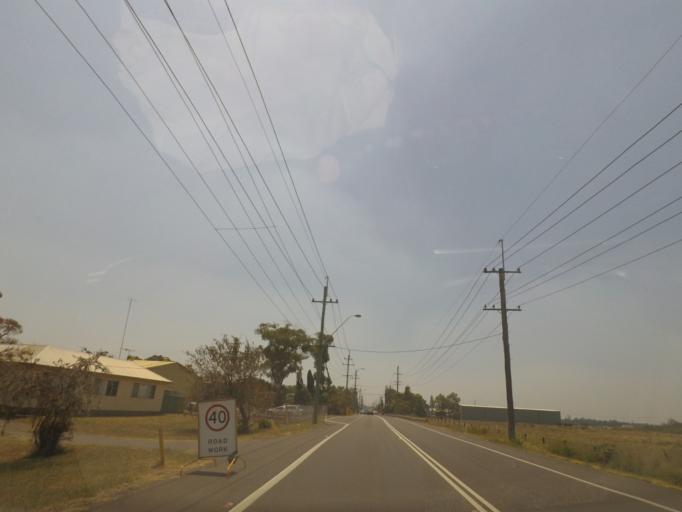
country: AU
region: New South Wales
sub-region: Newcastle
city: Mayfield West
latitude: -32.8262
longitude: 151.7389
